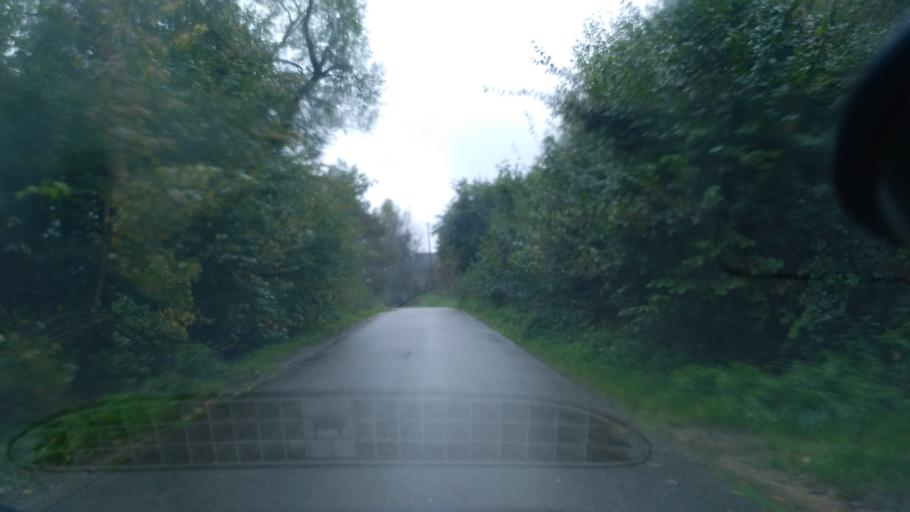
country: PL
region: Subcarpathian Voivodeship
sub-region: Powiat ropczycko-sedziszowski
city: Niedzwiada
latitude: 50.0090
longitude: 21.5491
